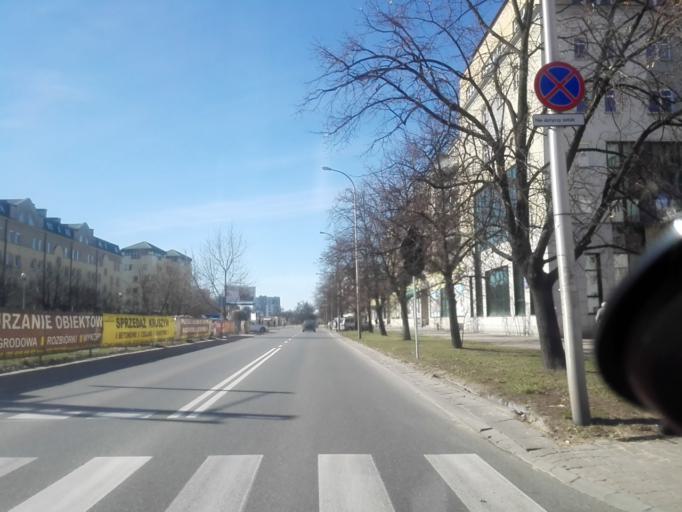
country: PL
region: Masovian Voivodeship
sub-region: Warszawa
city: Ochota
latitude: 52.1984
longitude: 20.9809
